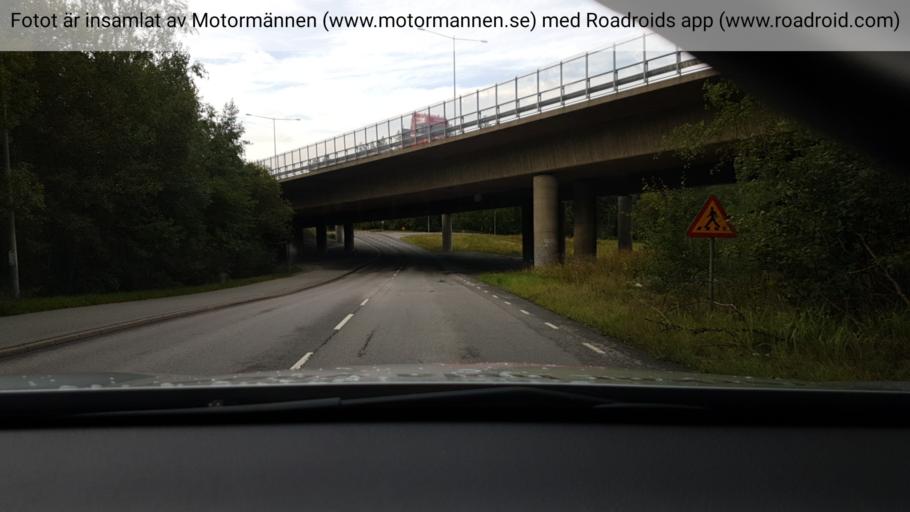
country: SE
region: Stockholm
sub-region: Haninge Kommun
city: Haninge
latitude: 59.1913
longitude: 18.1441
